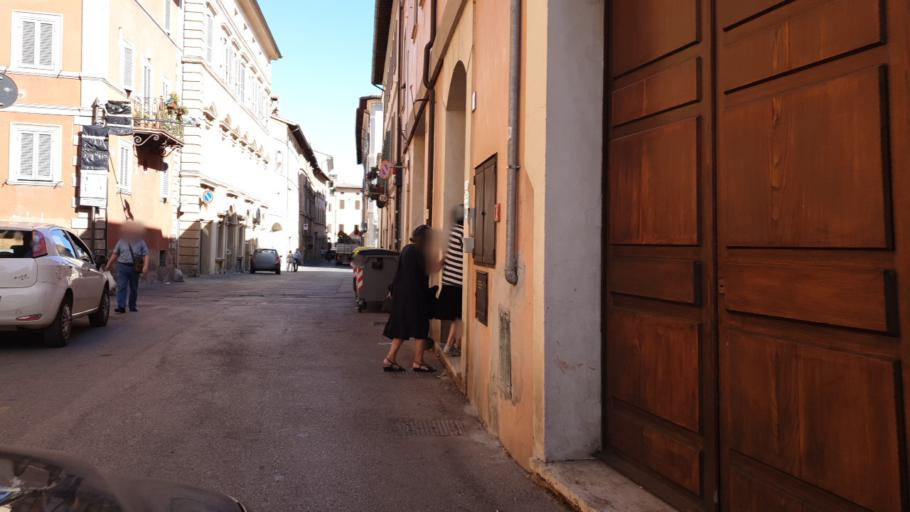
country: IT
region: Umbria
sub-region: Provincia di Perugia
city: Foligno
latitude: 42.9533
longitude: 12.7036
